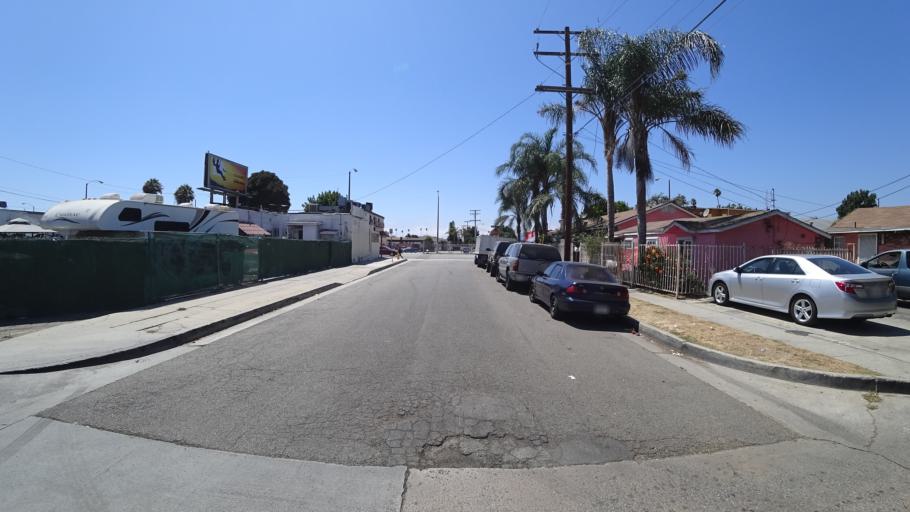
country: US
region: California
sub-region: Los Angeles County
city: Lennox
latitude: 33.9408
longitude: -118.3432
